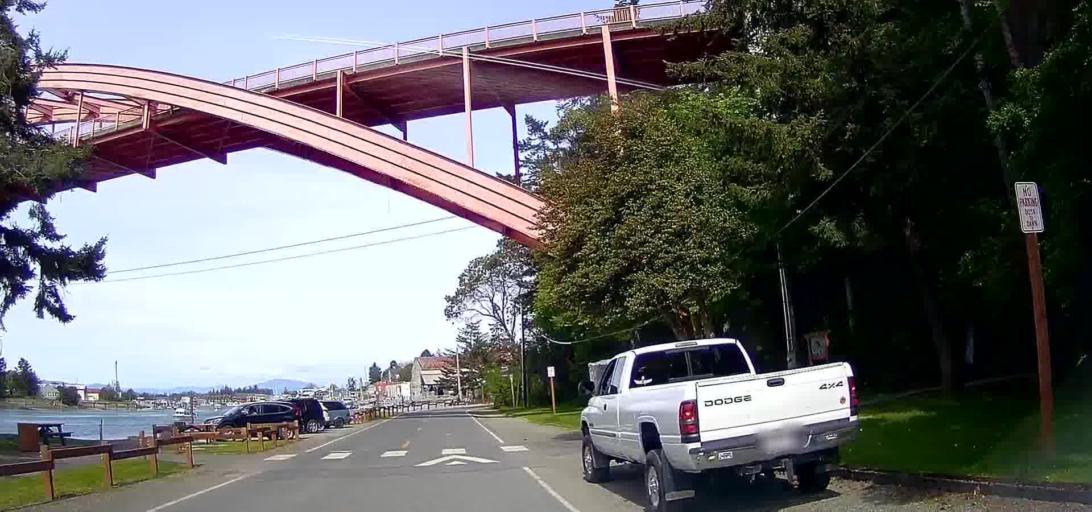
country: US
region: Washington
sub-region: Skagit County
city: Anacortes
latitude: 48.3858
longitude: -122.5024
